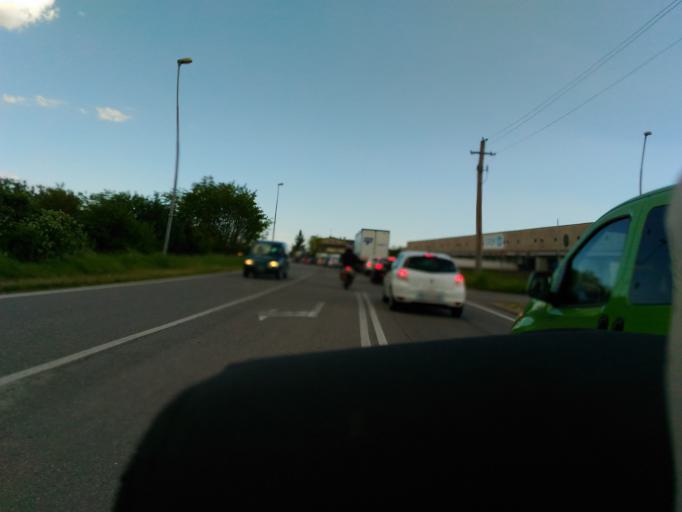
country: IT
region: Lombardy
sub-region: Citta metropolitana di Milano
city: Colturano
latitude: 45.3860
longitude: 9.3349
